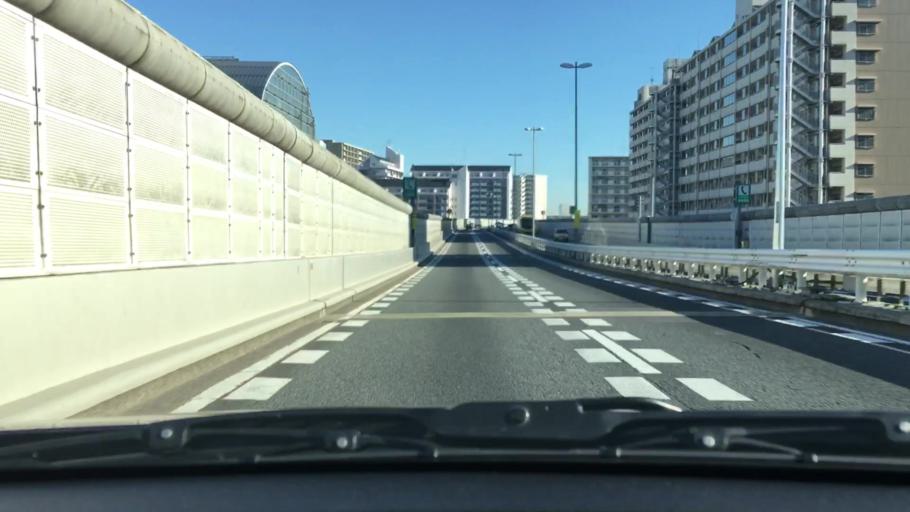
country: JP
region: Tokyo
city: Urayasu
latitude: 35.6959
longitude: 139.8485
